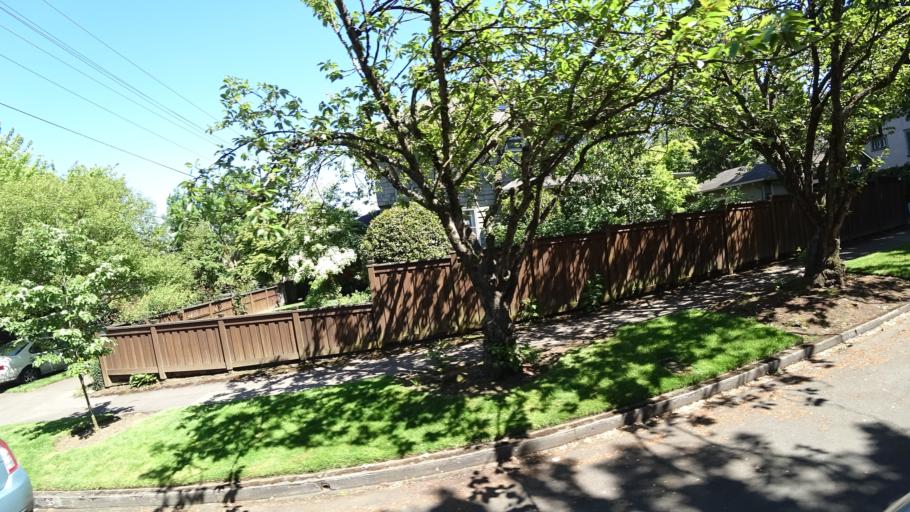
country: US
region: Oregon
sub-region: Multnomah County
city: Portland
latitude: 45.5155
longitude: -122.6371
